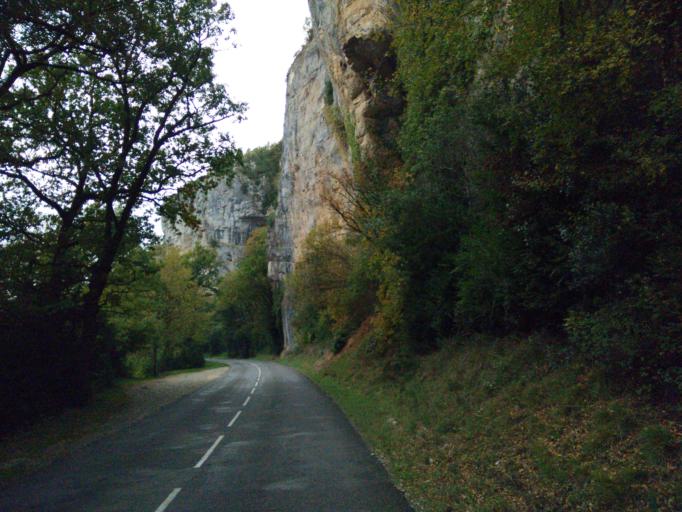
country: FR
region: Midi-Pyrenees
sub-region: Departement du Lot
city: Lalbenque
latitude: 44.4871
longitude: 1.6508
